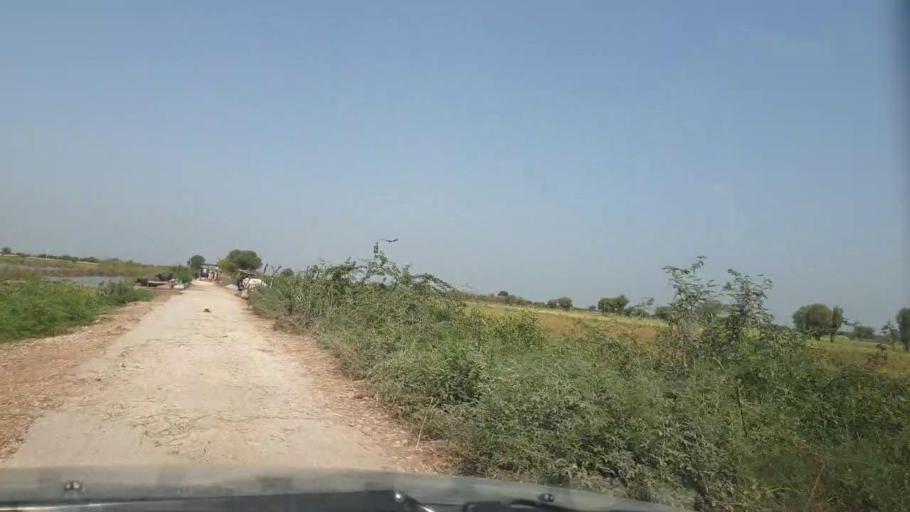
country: PK
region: Sindh
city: Tando Ghulam Ali
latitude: 25.0800
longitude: 68.8020
